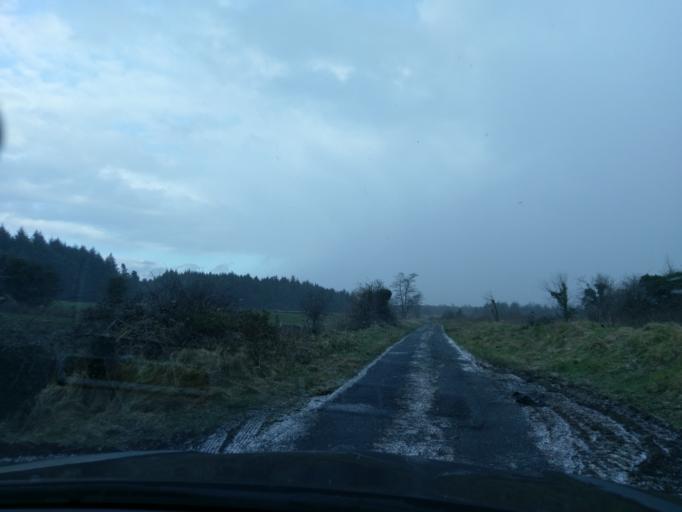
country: IE
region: Connaught
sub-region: County Galway
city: Athenry
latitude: 53.4048
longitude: -8.5927
